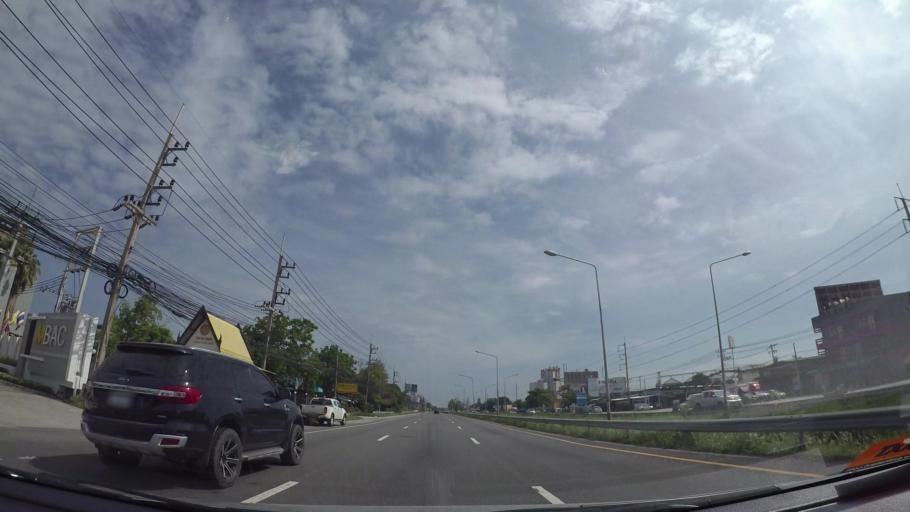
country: TH
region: Chon Buri
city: Si Racha
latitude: 13.2229
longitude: 100.9395
